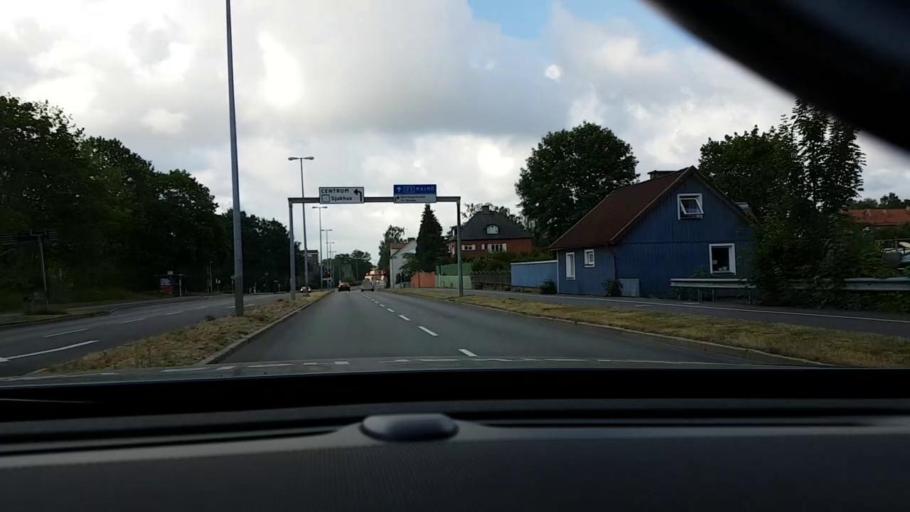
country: SE
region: Skane
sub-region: Hassleholms Kommun
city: Hassleholm
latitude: 56.1640
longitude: 13.7581
